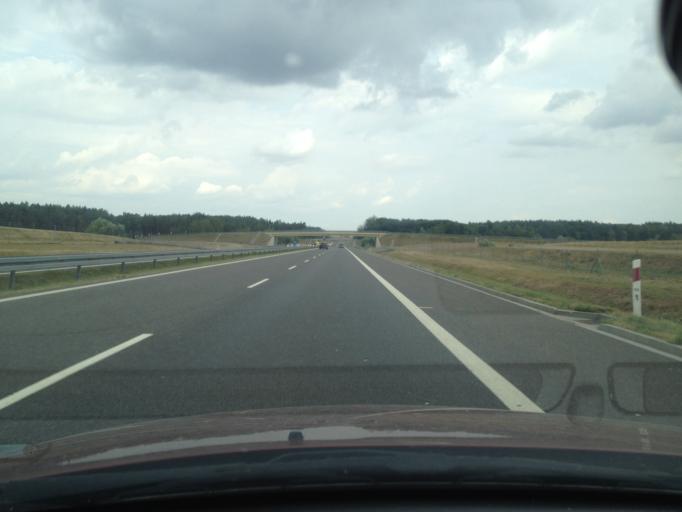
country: PL
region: West Pomeranian Voivodeship
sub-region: Powiat mysliborski
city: Mysliborz
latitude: 53.0045
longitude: 14.8620
